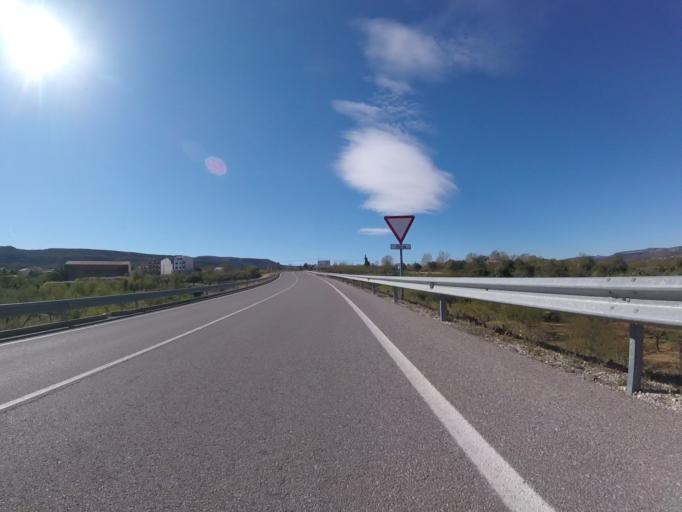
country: ES
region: Valencia
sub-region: Provincia de Castello
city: Albocasser
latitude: 40.3595
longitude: 0.0192
